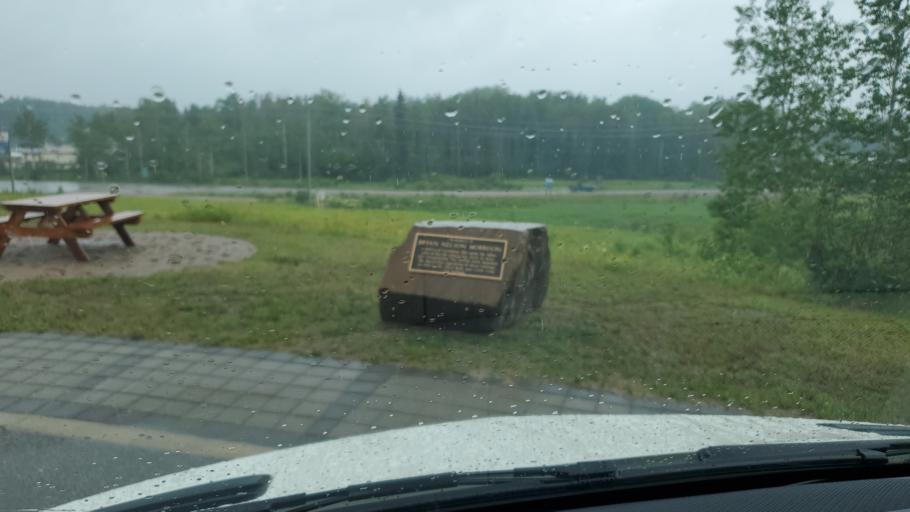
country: CA
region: Ontario
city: Greenstone
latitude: 49.6816
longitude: -86.9408
